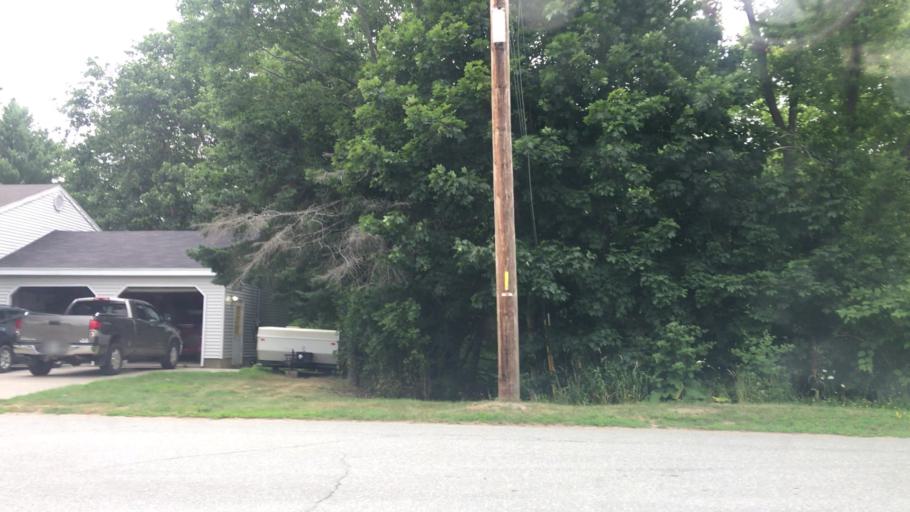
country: US
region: Maine
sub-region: Penobscot County
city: Brewer
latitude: 44.7742
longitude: -68.7690
